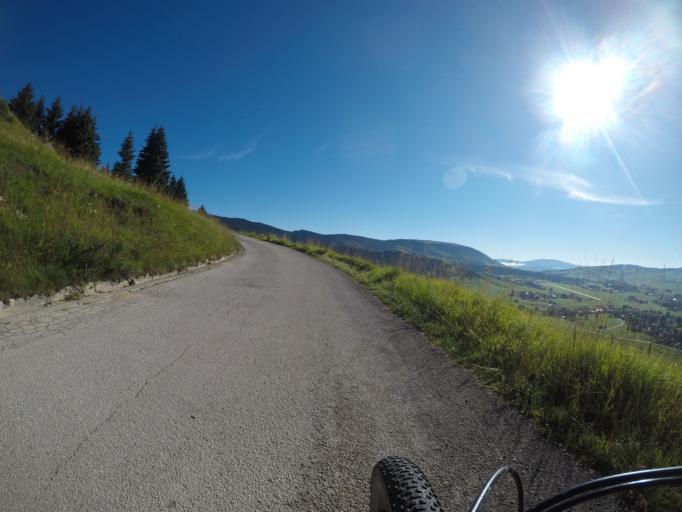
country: IT
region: Veneto
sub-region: Provincia di Vicenza
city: Canove di Roana
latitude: 45.8890
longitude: 11.4834
